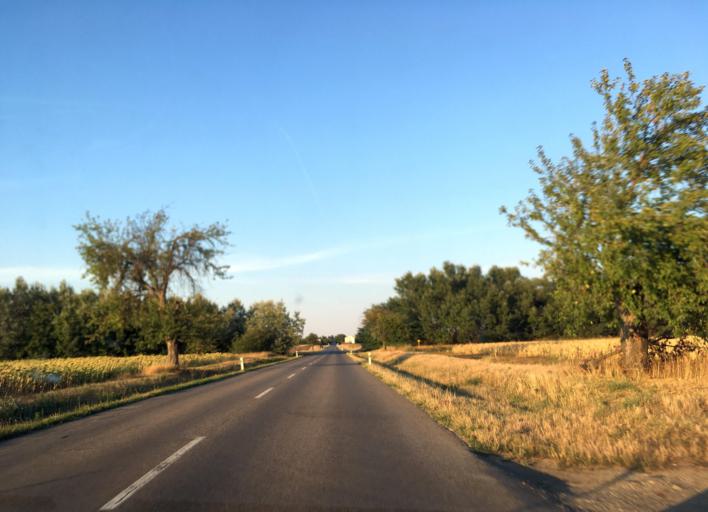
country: HU
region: Komarom-Esztergom
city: Dunaalmas
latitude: 47.7967
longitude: 18.3065
